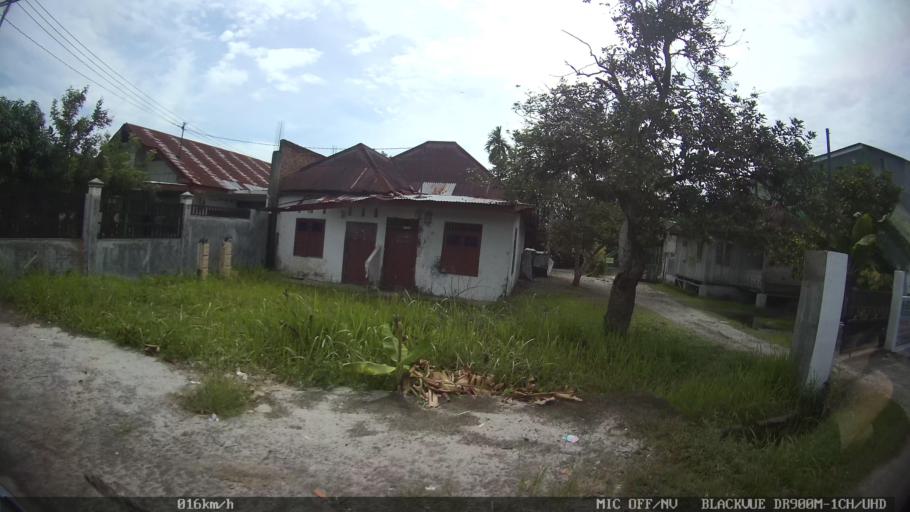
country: ID
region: North Sumatra
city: Percut
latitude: 3.6179
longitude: 98.7993
